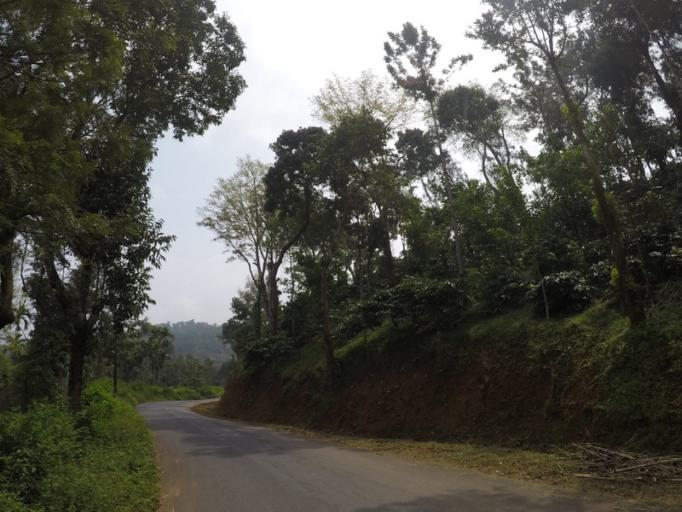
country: IN
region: Karnataka
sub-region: Chikmagalur
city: Mudigere
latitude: 13.1707
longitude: 75.4337
